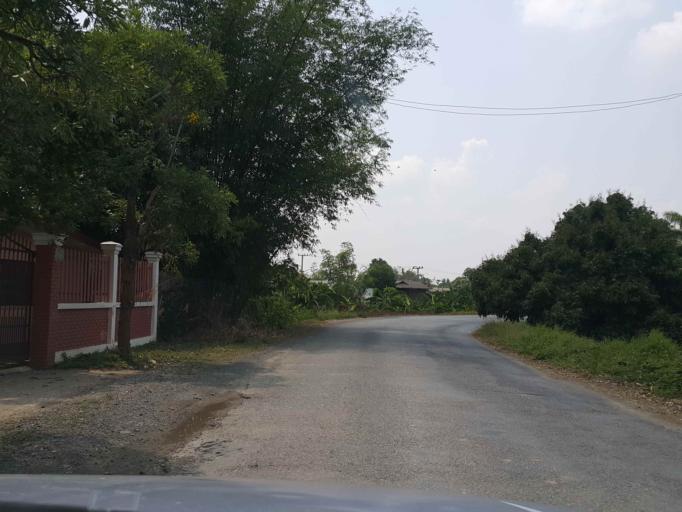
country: TH
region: Chiang Mai
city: Saraphi
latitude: 18.6767
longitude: 99.0067
